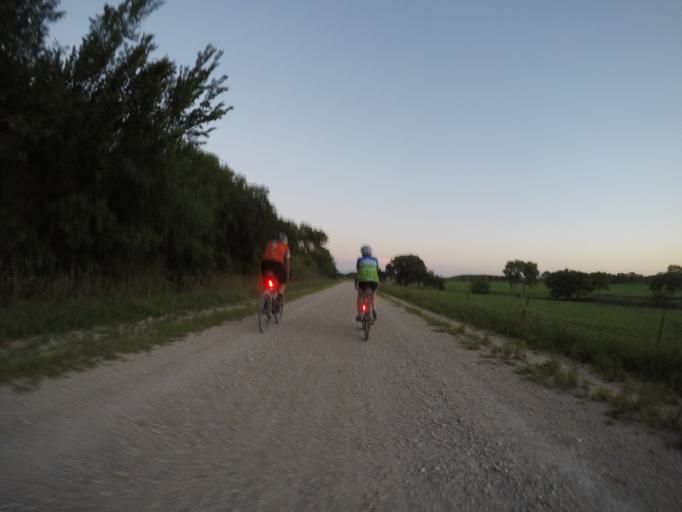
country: US
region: Kansas
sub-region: Riley County
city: Ogden
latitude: 38.9760
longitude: -96.5631
